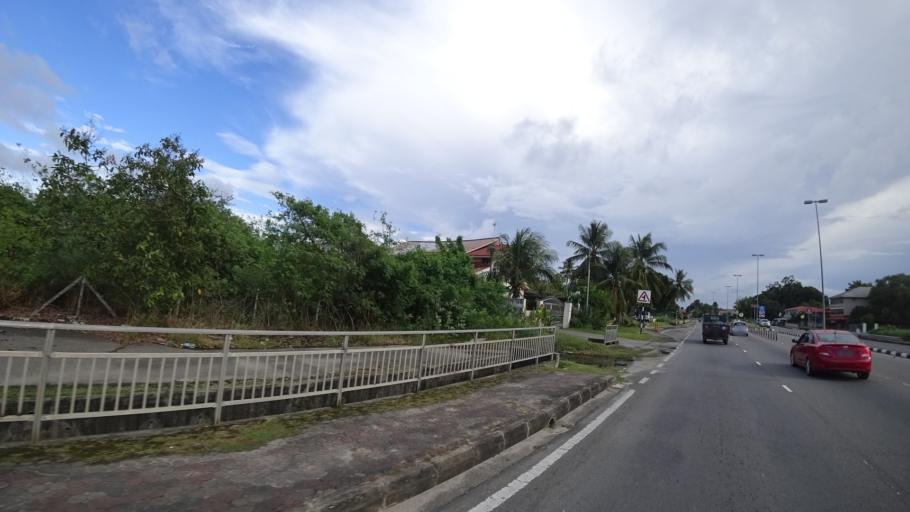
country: BN
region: Brunei and Muara
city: Bandar Seri Begawan
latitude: 4.8752
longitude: 114.8608
